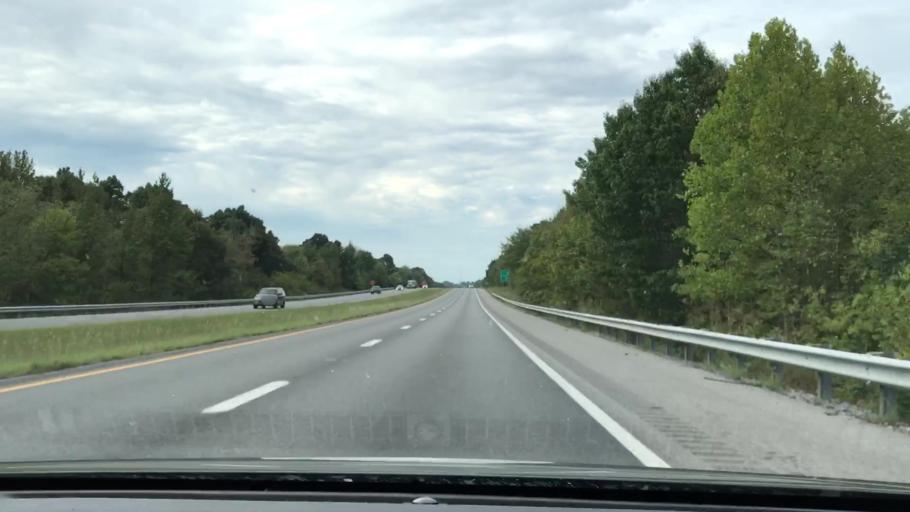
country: US
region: Kentucky
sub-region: Marshall County
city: Calvert City
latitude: 36.9636
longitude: -88.3482
